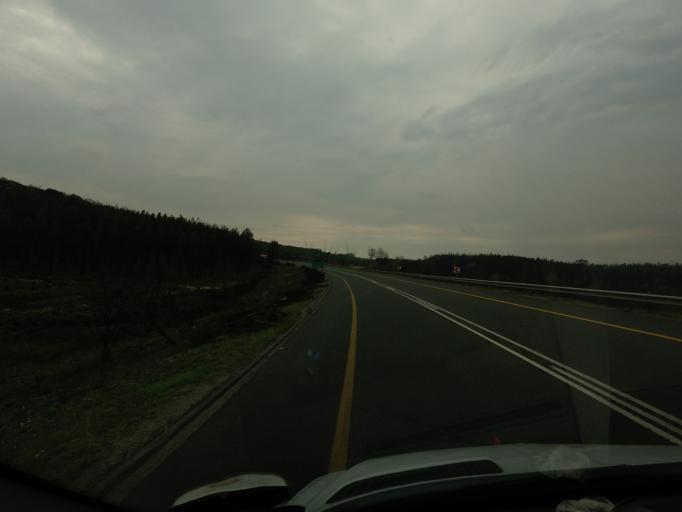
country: ZA
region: Western Cape
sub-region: Eden District Municipality
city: Knysna
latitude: -34.0361
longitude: 23.1558
